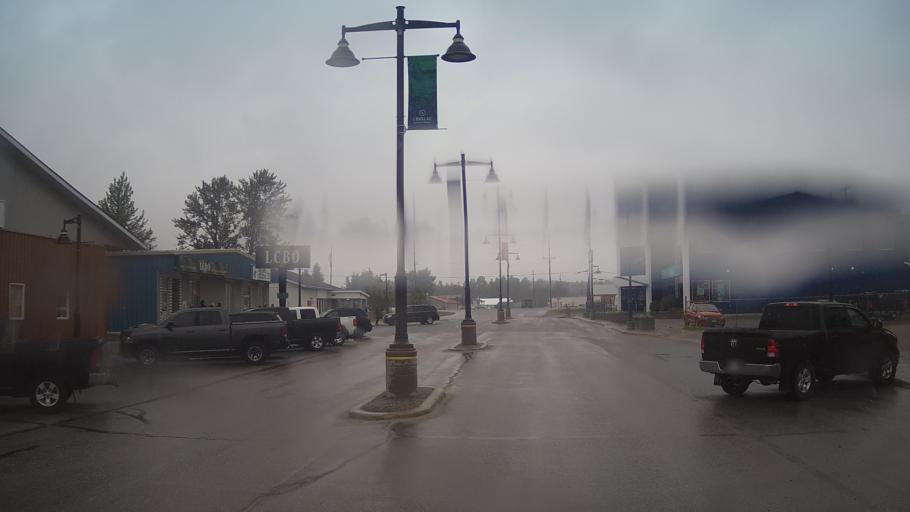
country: CA
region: Ontario
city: Greenstone
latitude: 49.7803
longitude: -86.5351
